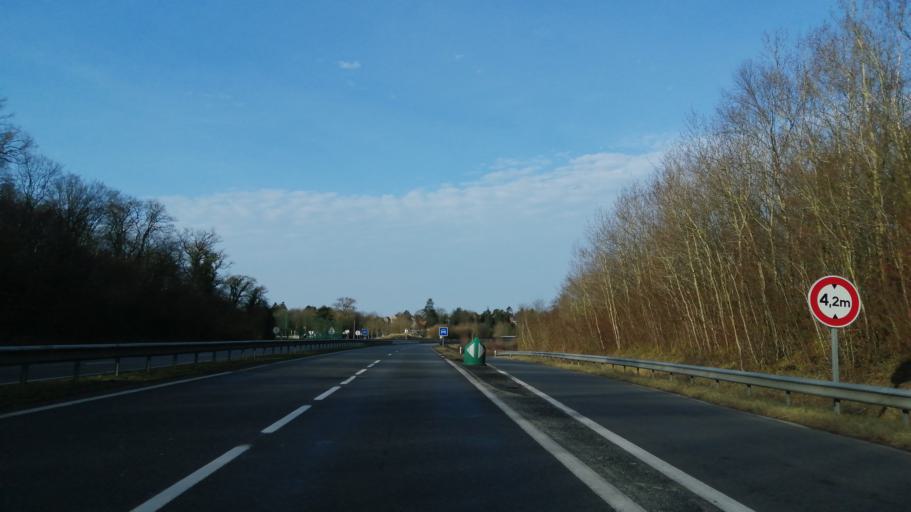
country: FR
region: Nord-Pas-de-Calais
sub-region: Departement du Pas-de-Calais
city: La Capelle-les-Boulogne
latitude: 50.7323
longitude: 1.7199
